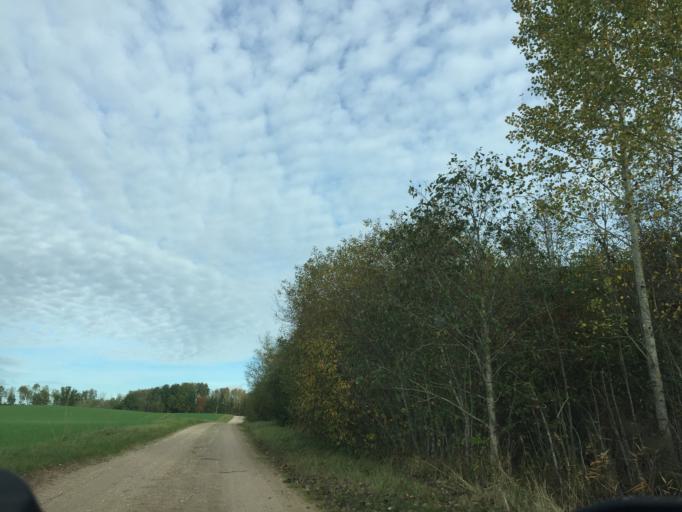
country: LV
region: Jaunpils
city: Jaunpils
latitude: 56.6331
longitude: 23.0686
